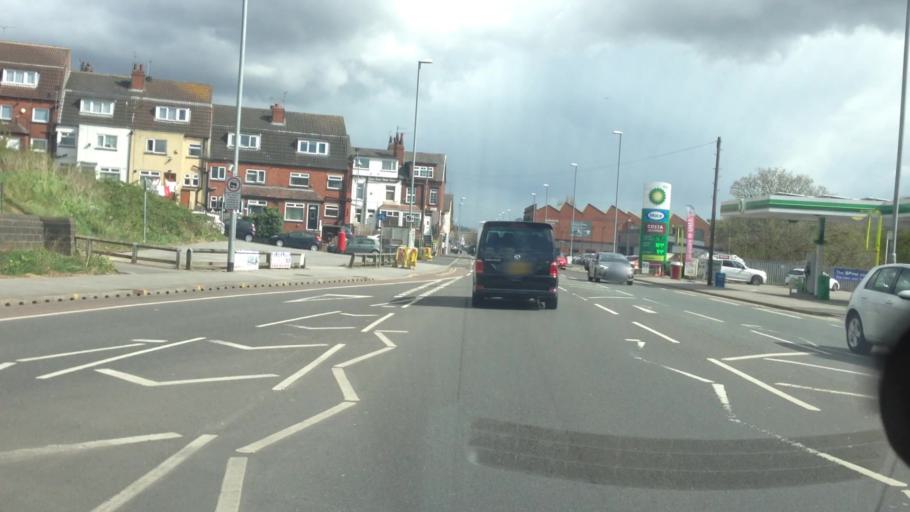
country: GB
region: England
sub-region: City and Borough of Leeds
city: Leeds
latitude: 53.8092
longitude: -1.5905
